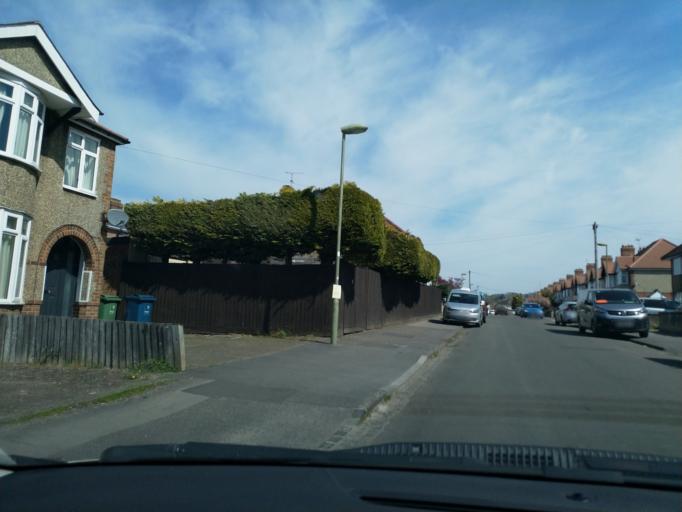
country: GB
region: England
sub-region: Oxfordshire
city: Cowley
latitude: 51.7364
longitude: -1.2050
